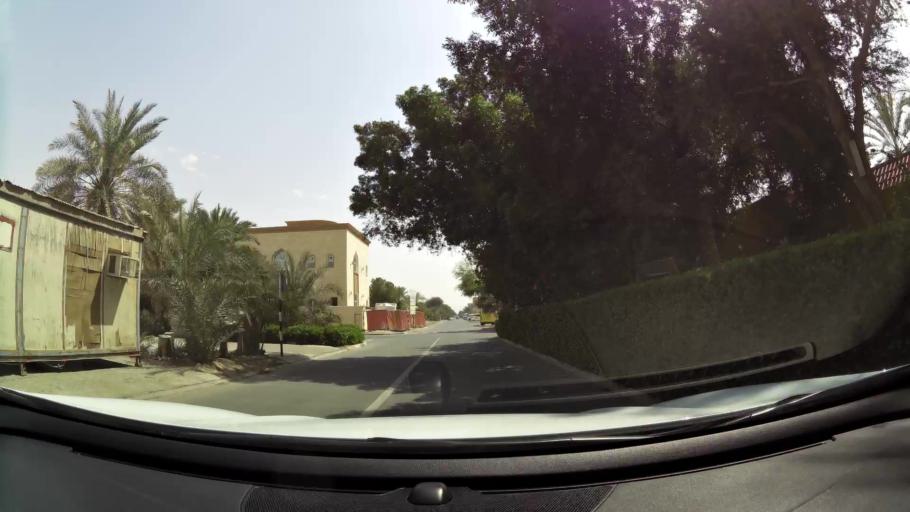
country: AE
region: Abu Dhabi
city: Abu Dhabi
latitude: 24.2954
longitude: 54.6326
